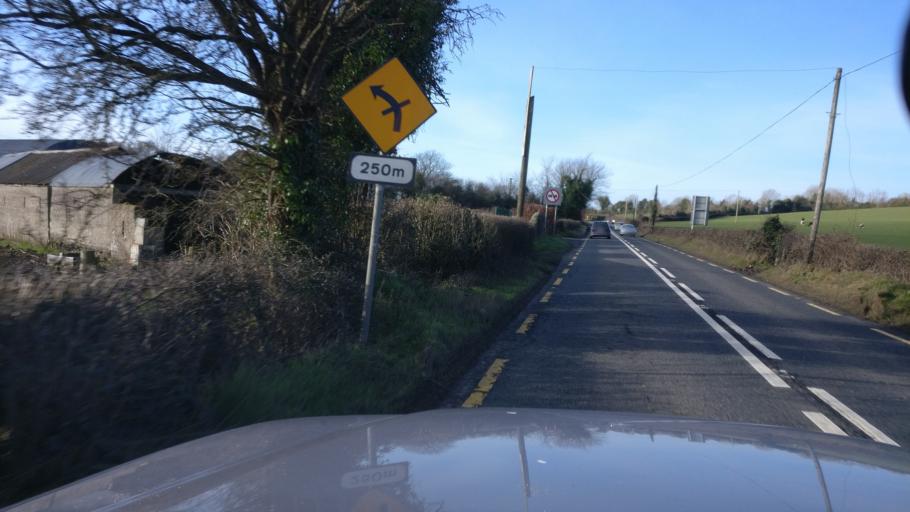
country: IE
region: Leinster
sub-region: Uibh Fhaili
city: Tullamore
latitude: 53.1959
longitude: -7.4163
